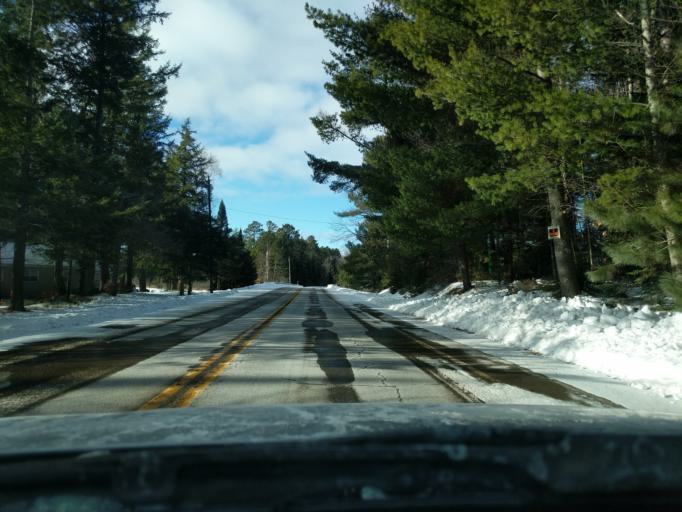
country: US
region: Wisconsin
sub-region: Vilas County
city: Eagle River
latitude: 45.7718
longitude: -89.0694
